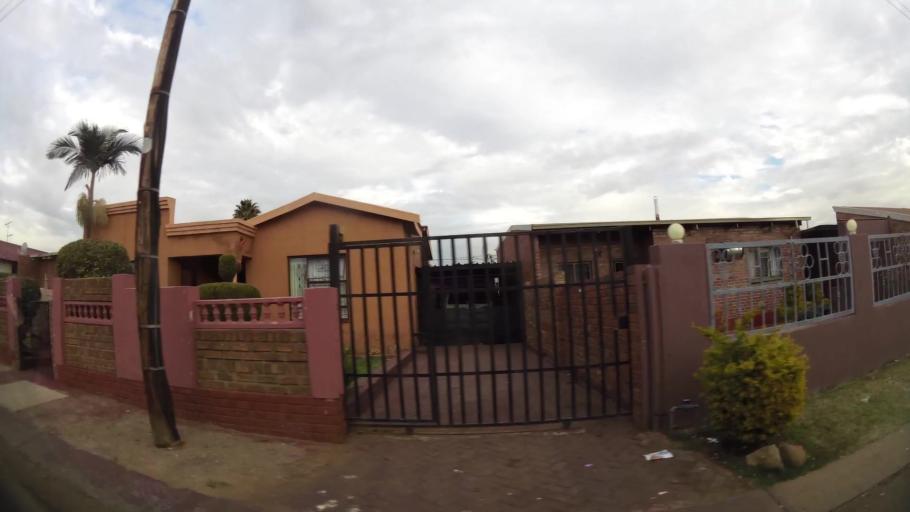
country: ZA
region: Gauteng
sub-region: City of Tshwane Metropolitan Municipality
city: Pretoria
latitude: -25.7053
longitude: 28.3128
